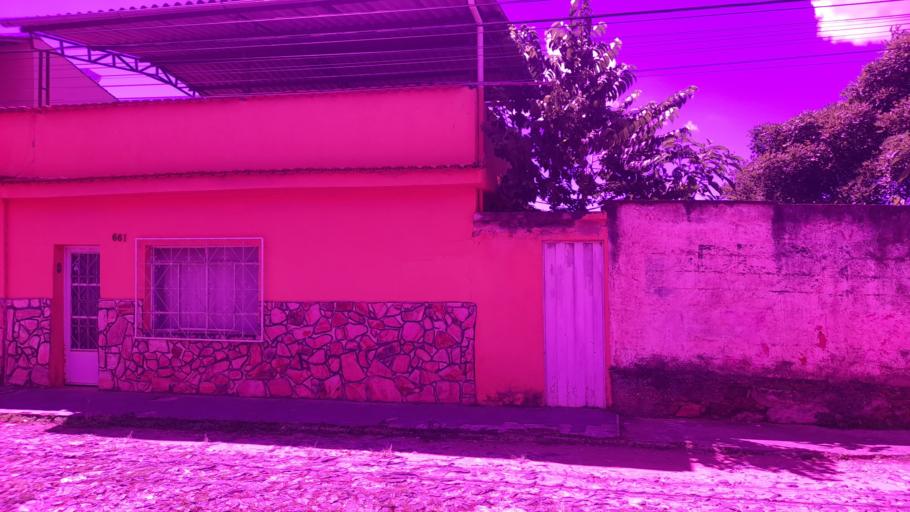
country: BR
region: Minas Gerais
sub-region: Sao Joao Del Rei
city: Sao Joao del Rei
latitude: -21.1381
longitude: -44.2690
